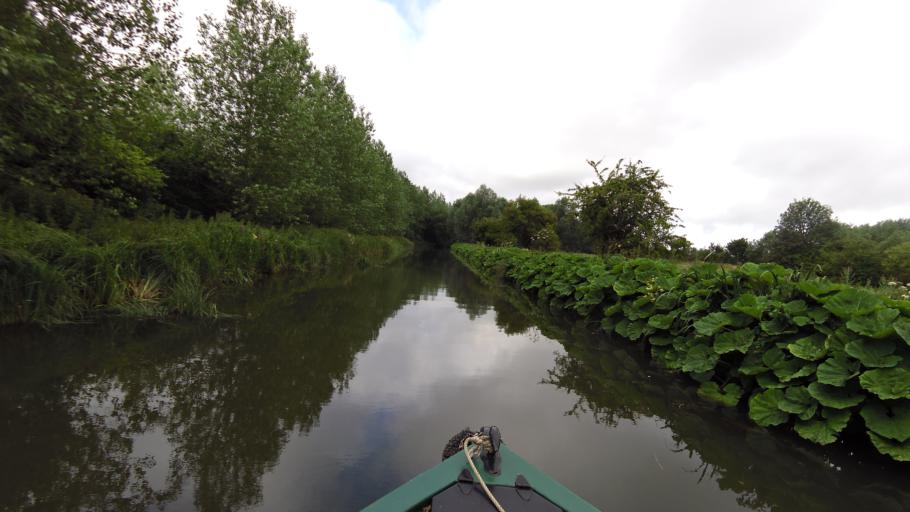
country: GB
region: England
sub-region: West Berkshire
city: Thatcham
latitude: 51.3945
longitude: -1.1887
